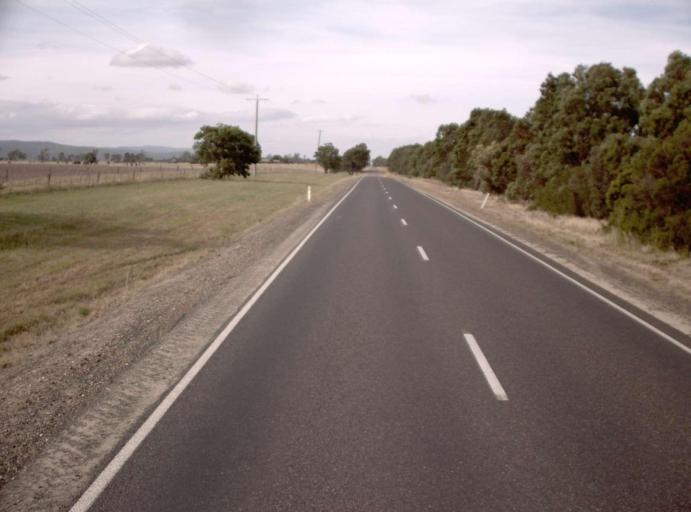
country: AU
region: Victoria
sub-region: Wellington
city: Heyfield
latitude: -38.0470
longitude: 146.6645
